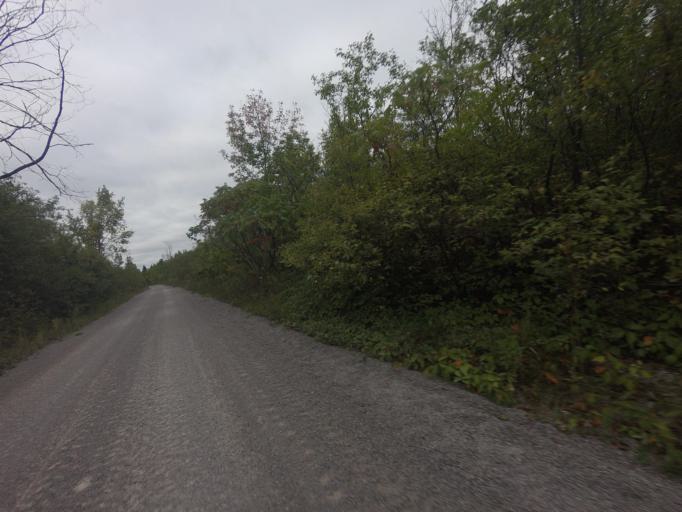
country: CA
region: Ontario
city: Omemee
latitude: 44.5194
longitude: -78.7331
